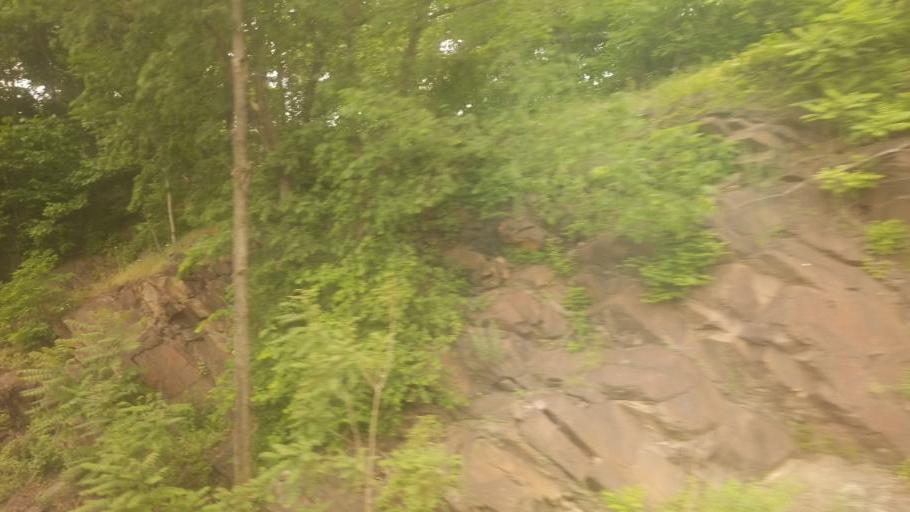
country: US
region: West Virginia
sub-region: Morgan County
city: Berkeley Springs
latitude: 39.6118
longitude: -78.3710
